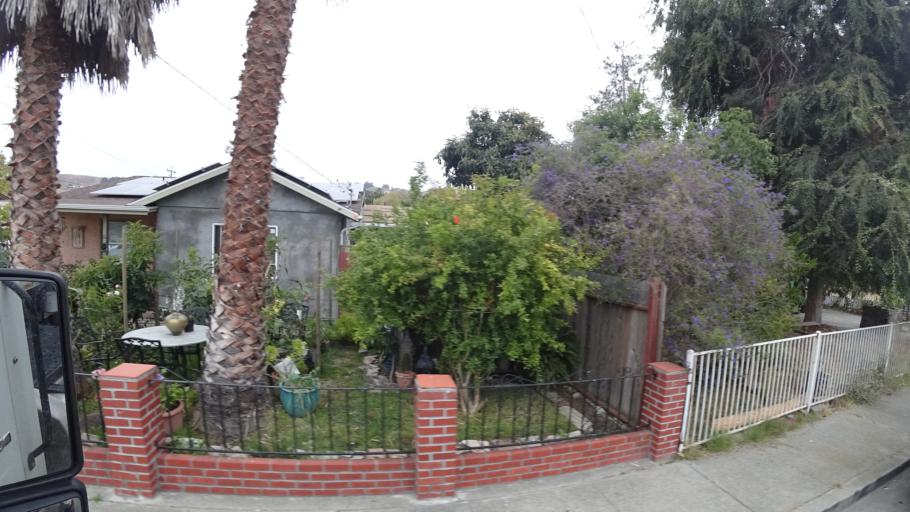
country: US
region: California
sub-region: Alameda County
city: Hayward
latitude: 37.6381
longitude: -122.0588
